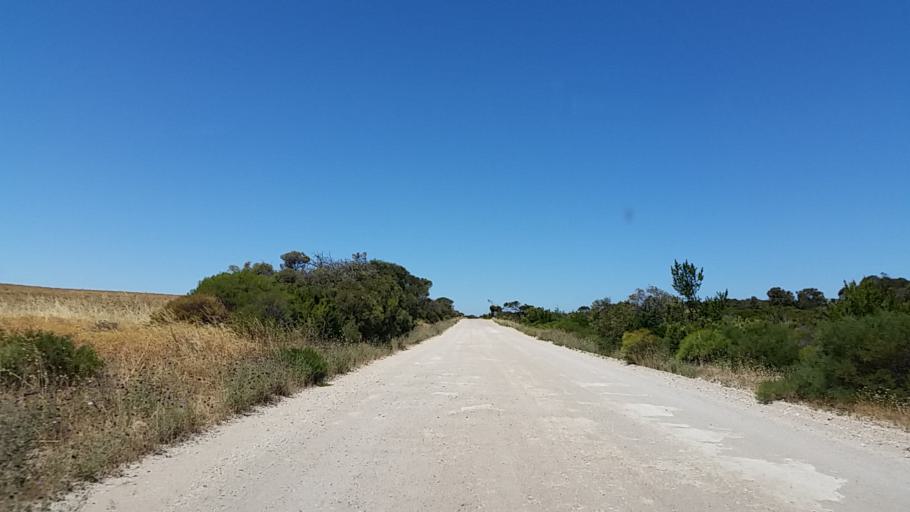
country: AU
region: South Australia
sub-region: Yorke Peninsula
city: Honiton
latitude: -35.1178
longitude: 137.3636
